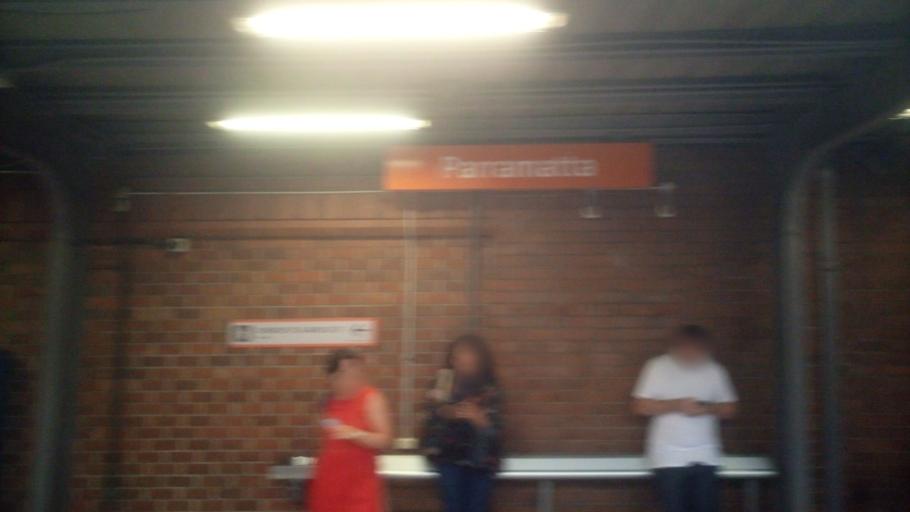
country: AU
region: New South Wales
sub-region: Parramatta
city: Paramatta
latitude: -33.8172
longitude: 151.0055
